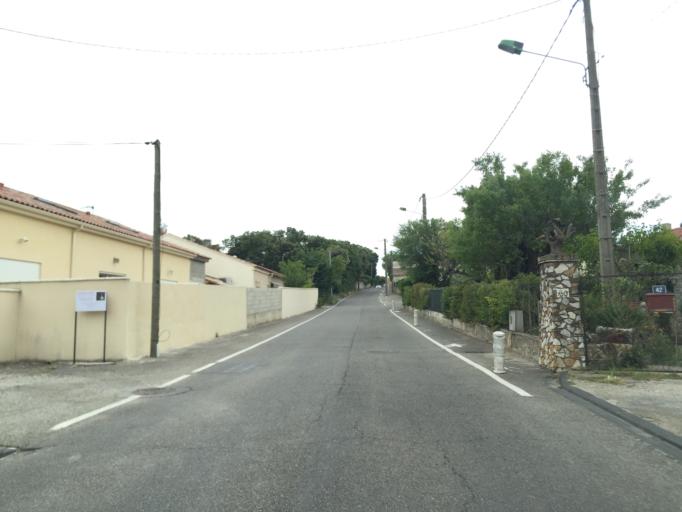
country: FR
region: Provence-Alpes-Cote d'Azur
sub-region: Departement du Vaucluse
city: Orange
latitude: 44.1224
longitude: 4.8266
